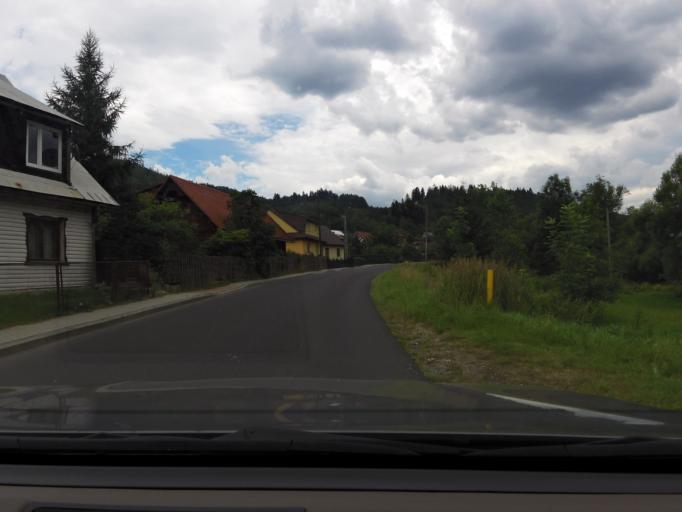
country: PL
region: Silesian Voivodeship
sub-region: Powiat zywiecki
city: Ujsoly
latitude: 49.4746
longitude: 19.1473
